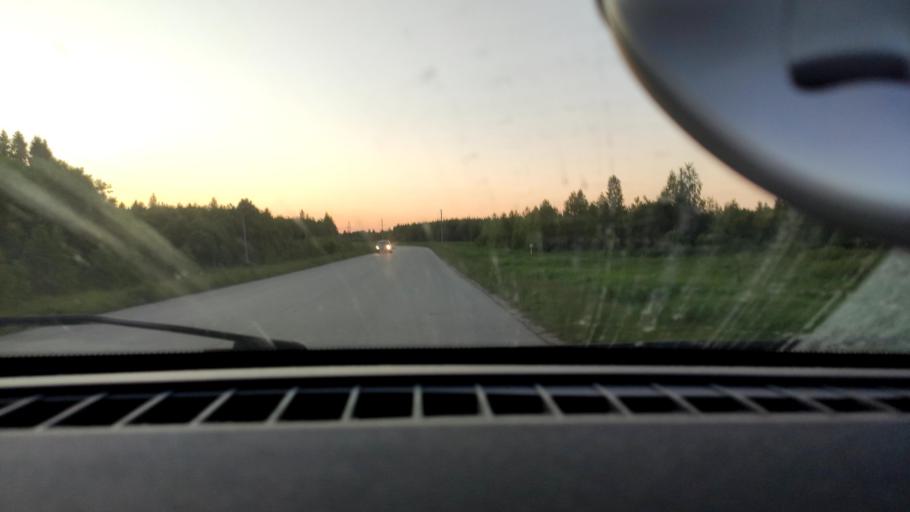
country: RU
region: Perm
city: Polazna
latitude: 58.2016
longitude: 56.5318
